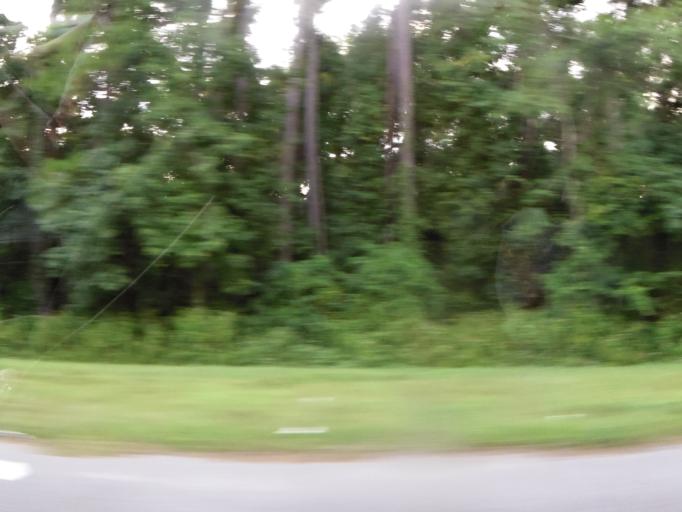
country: US
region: Georgia
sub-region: Glynn County
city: Dock Junction
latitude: 31.2279
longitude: -81.4972
